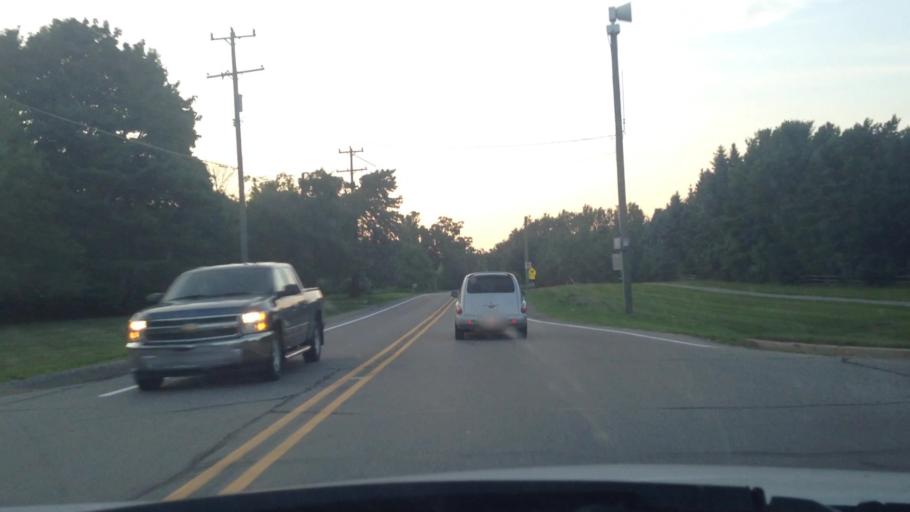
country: US
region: Michigan
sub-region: Oakland County
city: Lake Orion
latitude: 42.7482
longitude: -83.3084
